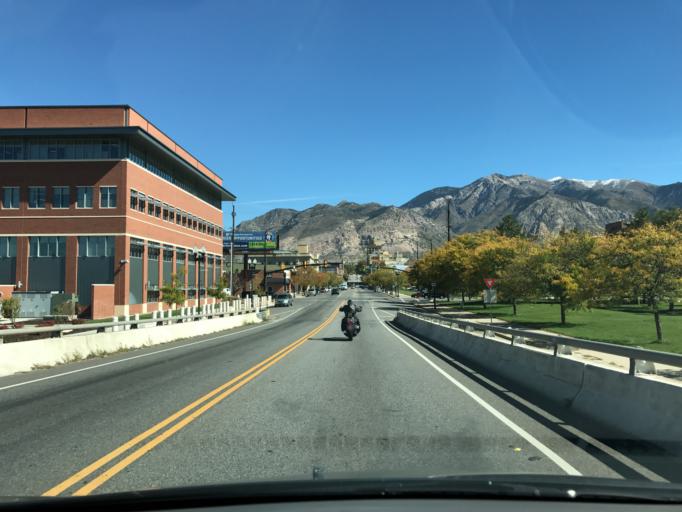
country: US
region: Utah
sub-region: Weber County
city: Ogden
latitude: 41.2228
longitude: -111.9770
